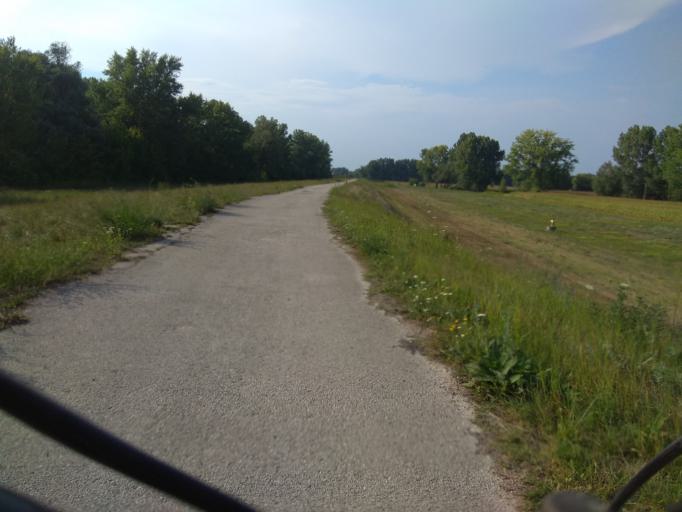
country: SK
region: Trnavsky
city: Gabcikovo
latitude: 47.8112
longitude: 17.6303
